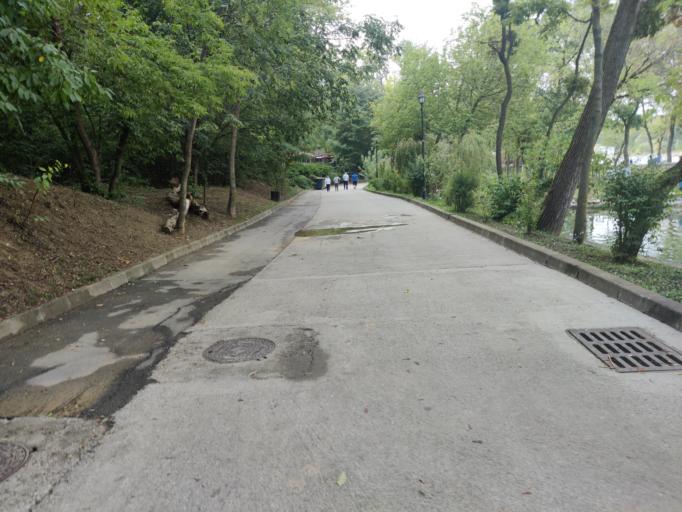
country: RO
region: Iasi
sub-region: Municipiul Iasi
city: Iasi
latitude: 47.1784
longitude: 27.6061
